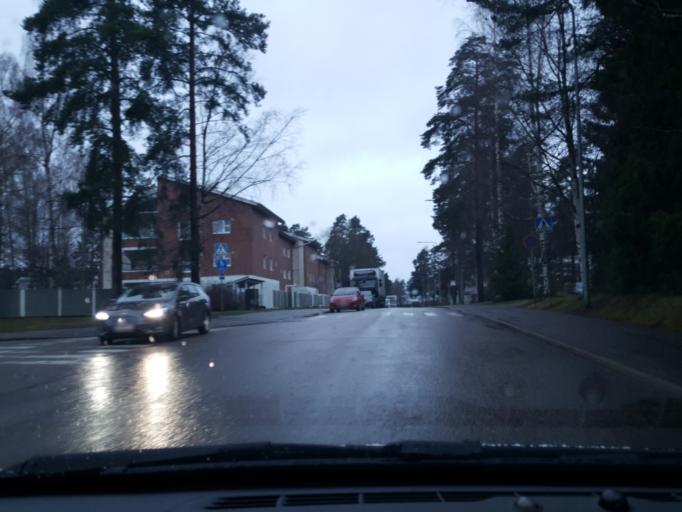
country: FI
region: Uusimaa
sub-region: Helsinki
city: Vantaa
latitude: 60.3046
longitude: 25.0488
